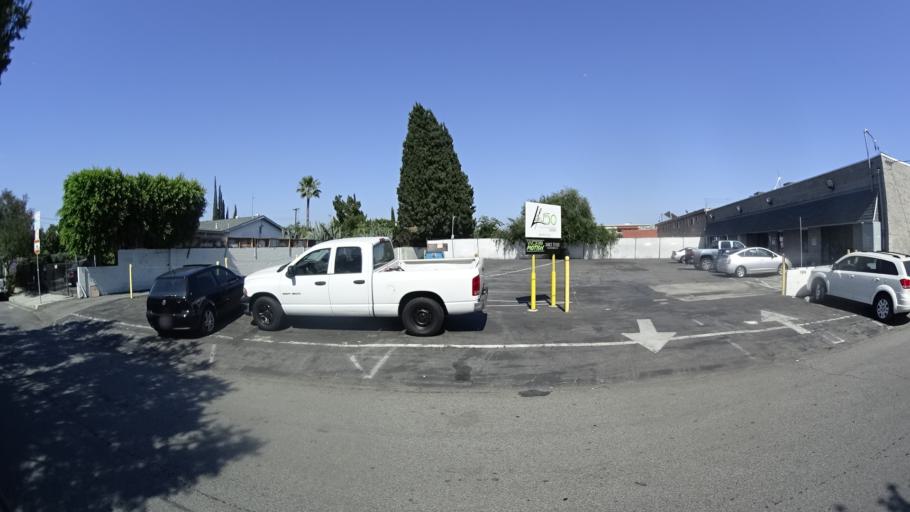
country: US
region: California
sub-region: Los Angeles County
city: Van Nuys
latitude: 34.2097
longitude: -118.4247
